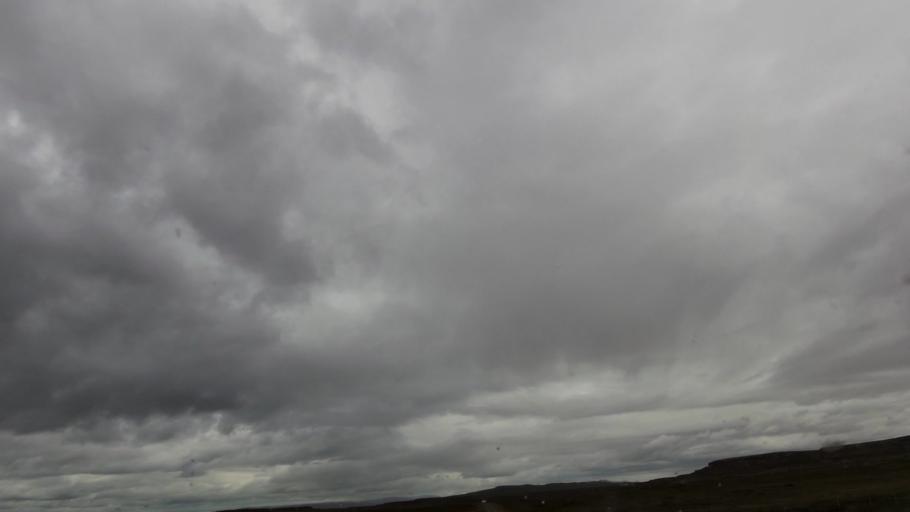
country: IS
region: West
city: Borgarnes
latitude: 65.0253
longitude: -22.1316
